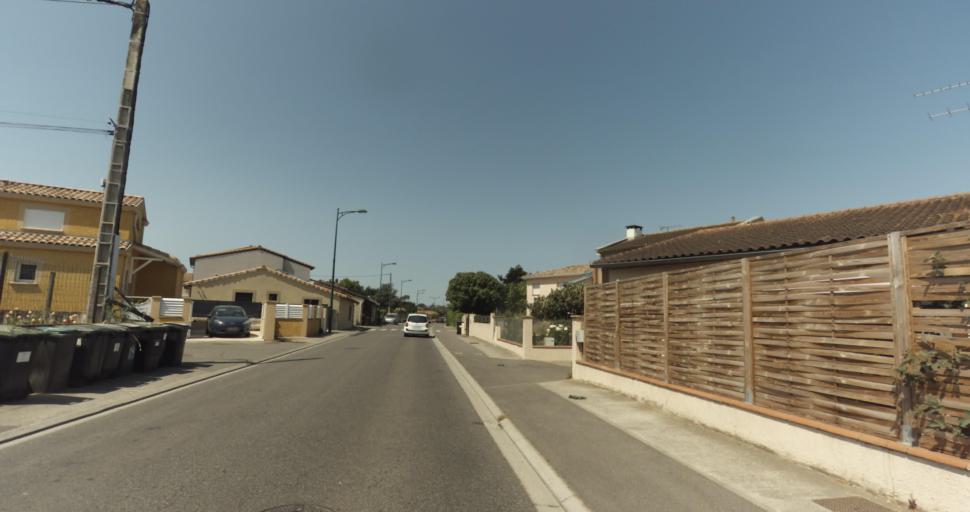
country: FR
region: Midi-Pyrenees
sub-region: Departement de la Haute-Garonne
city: Plaisance-du-Touch
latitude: 43.5606
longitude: 1.3030
